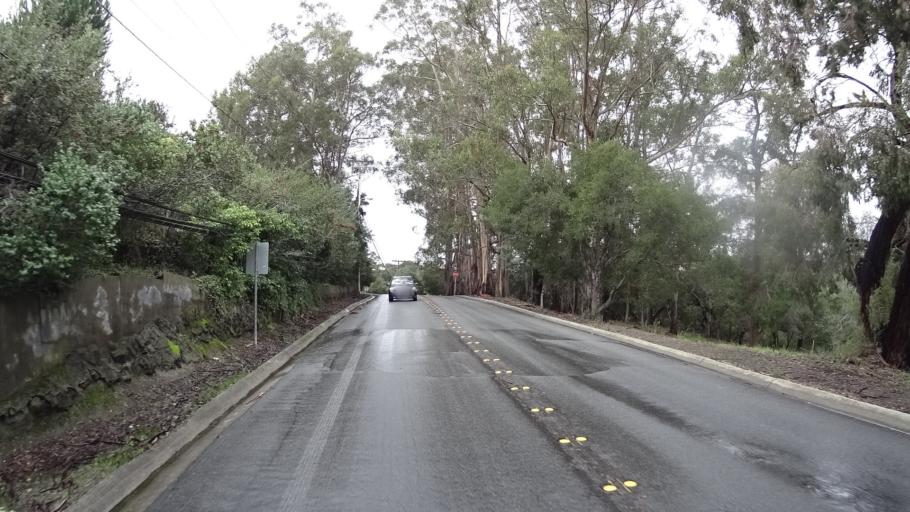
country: US
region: California
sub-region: San Mateo County
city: Hillsborough
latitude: 37.5595
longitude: -122.3726
